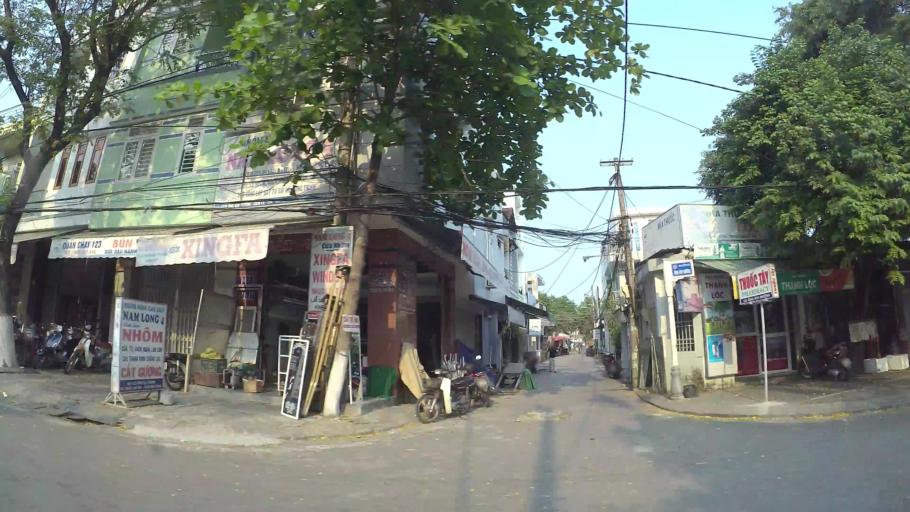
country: VN
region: Da Nang
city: Cam Le
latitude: 16.0188
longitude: 108.2039
